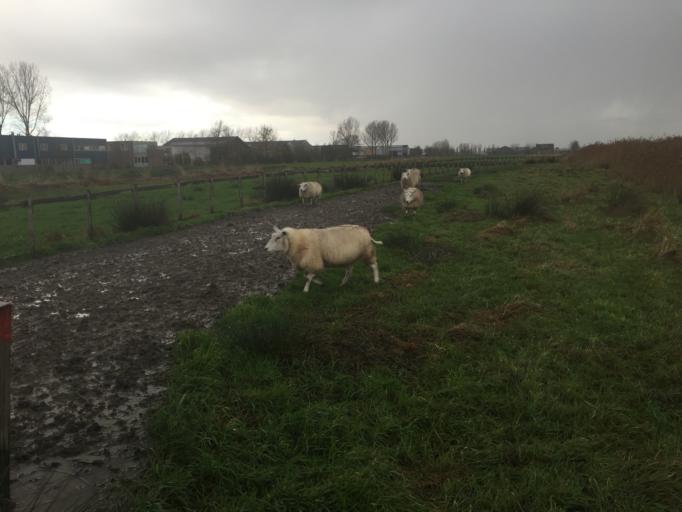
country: NL
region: South Holland
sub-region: Gemeente Nieuwkoop
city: Nieuwkoop
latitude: 52.1597
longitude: 4.7876
